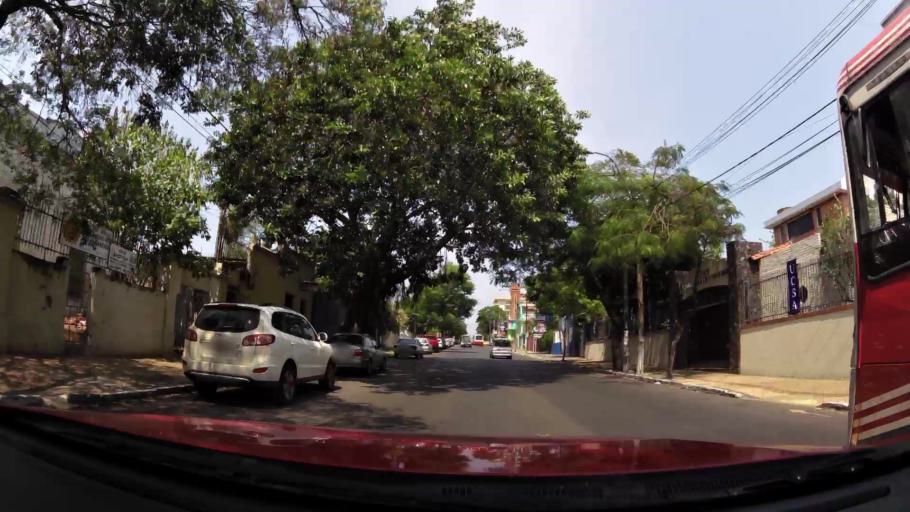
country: PY
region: Asuncion
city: Asuncion
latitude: -25.2855
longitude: -57.6464
